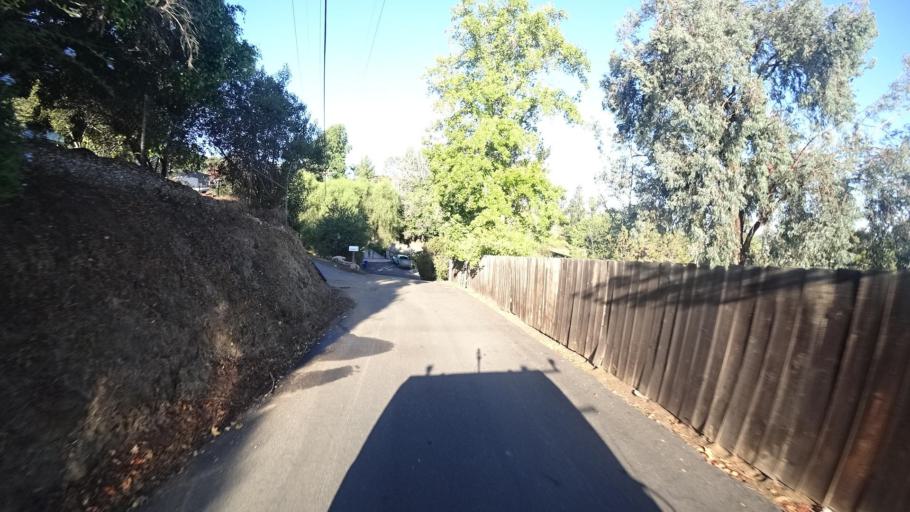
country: US
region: California
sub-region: San Diego County
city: Casa de Oro-Mount Helix
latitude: 32.7726
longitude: -116.9674
